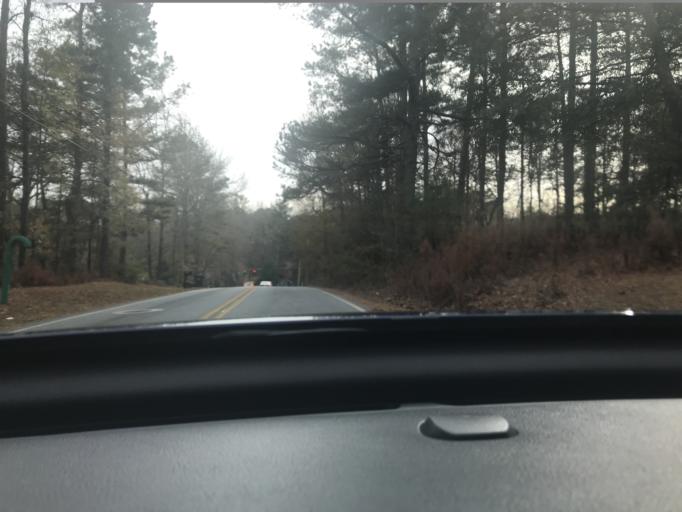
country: US
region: Georgia
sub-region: Gwinnett County
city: Lilburn
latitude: 33.8889
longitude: -84.0931
